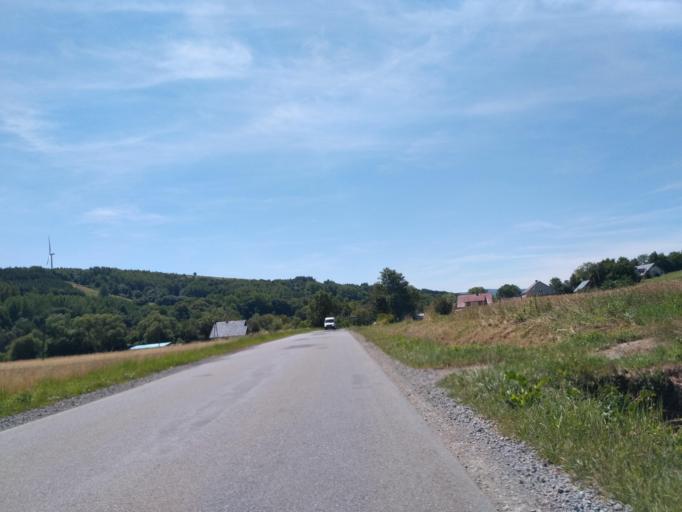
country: PL
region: Subcarpathian Voivodeship
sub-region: Powiat sanocki
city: Bukowsko
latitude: 49.5027
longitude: 22.0779
